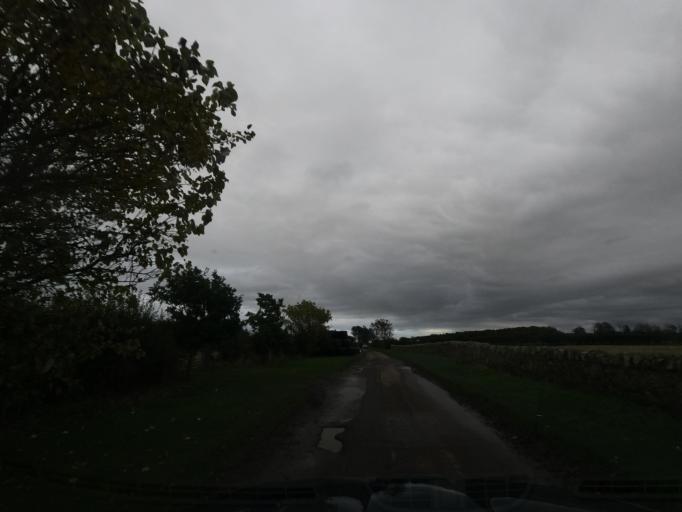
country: GB
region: England
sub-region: Northumberland
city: Ford
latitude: 55.6918
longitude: -2.0883
